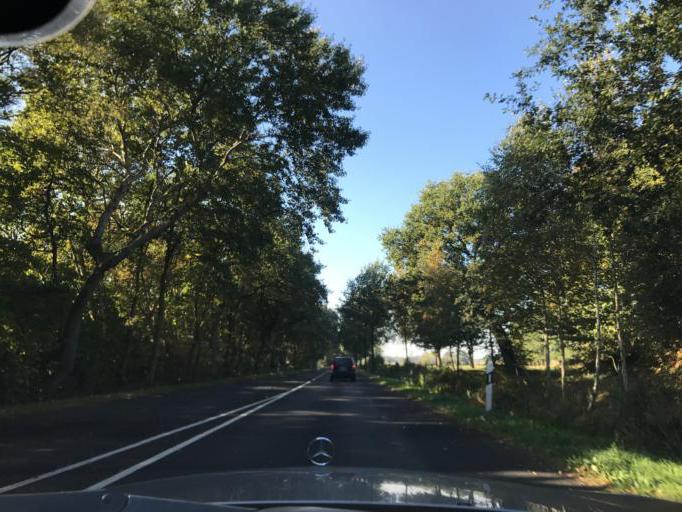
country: DE
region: Lower Saxony
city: Bunde
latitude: 53.1343
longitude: 7.2962
